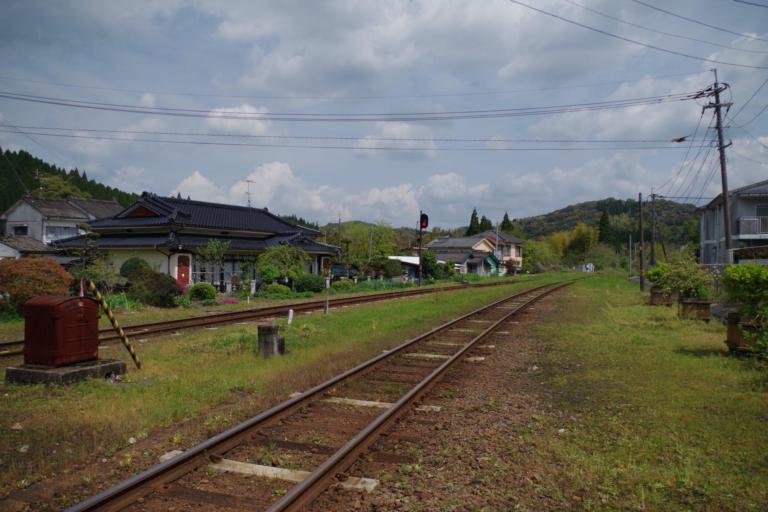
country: JP
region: Kagoshima
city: Kokubu-matsuki
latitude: 31.8693
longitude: 130.7345
